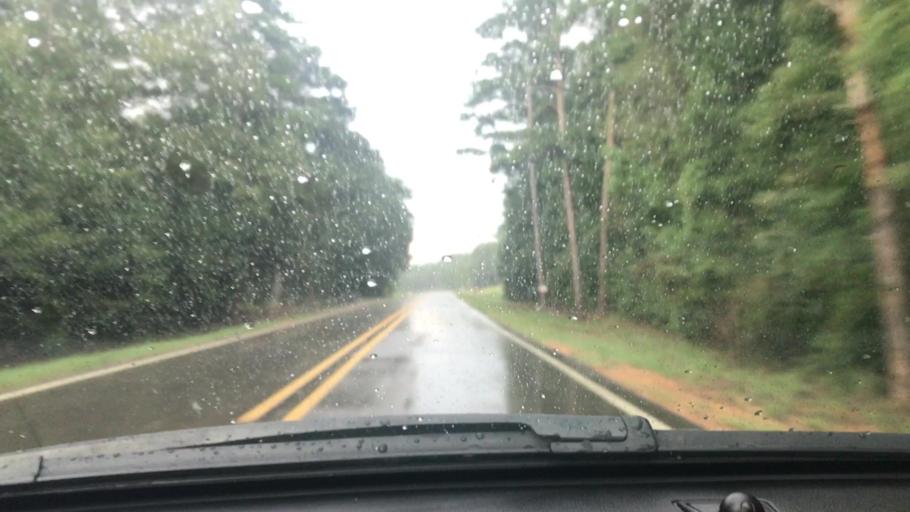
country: US
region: Mississippi
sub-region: Pike County
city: Summit
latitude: 31.3356
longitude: -90.5656
